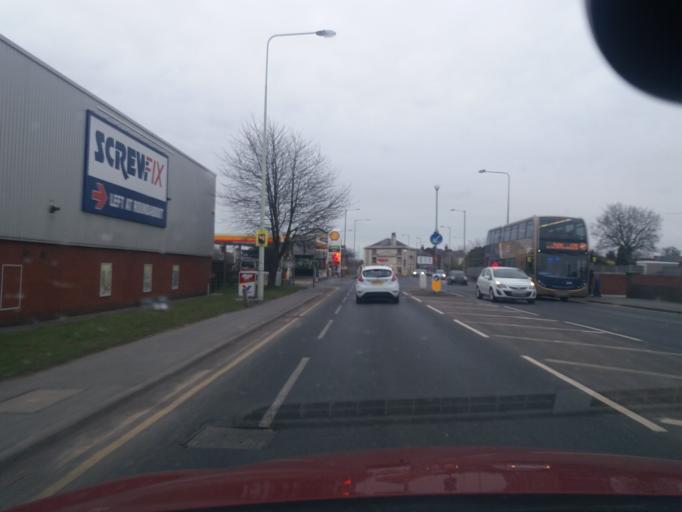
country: GB
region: England
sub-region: Lancashire
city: Chorley
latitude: 53.6626
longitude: -2.6314
